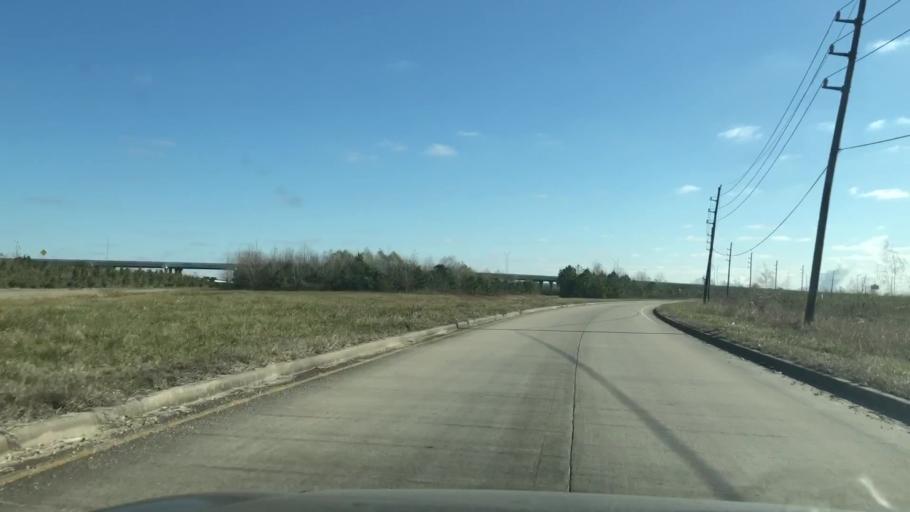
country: US
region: Texas
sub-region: Harris County
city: Cloverleaf
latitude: 29.8298
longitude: -95.1799
